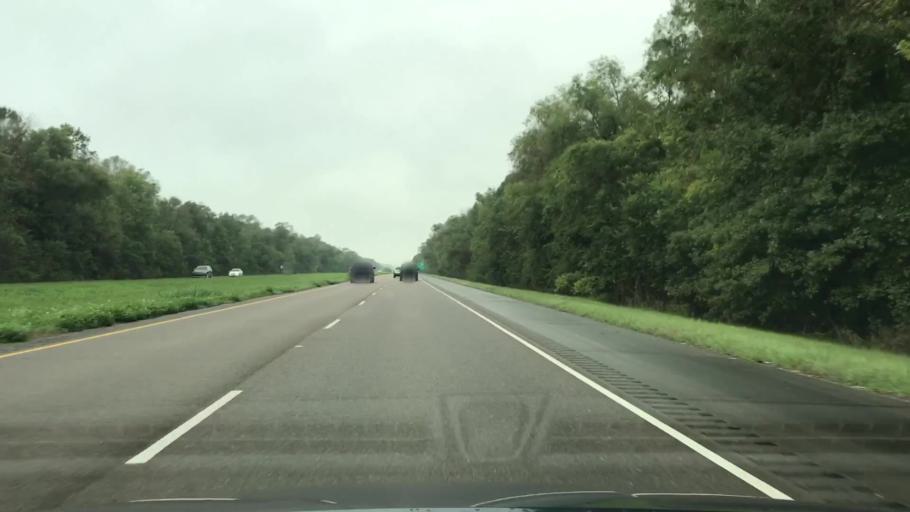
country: US
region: Louisiana
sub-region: Terrebonne Parish
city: Gray
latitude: 29.6846
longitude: -90.7312
